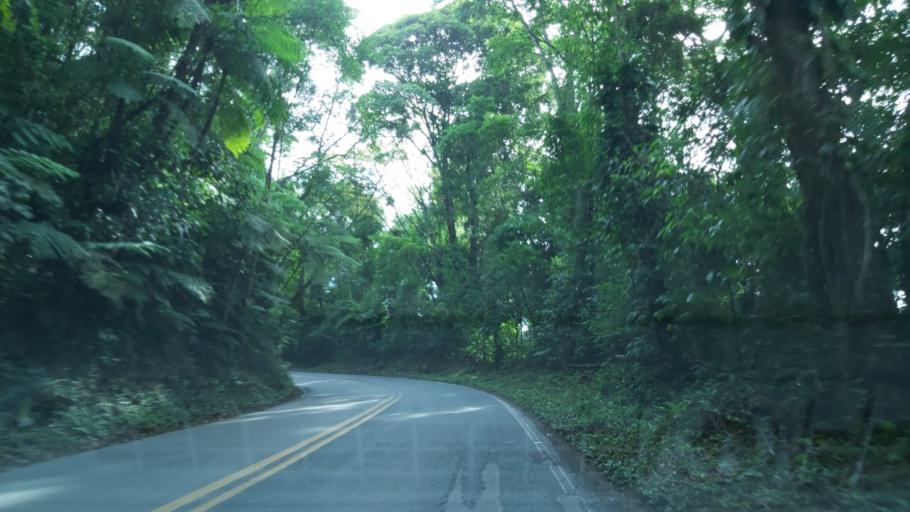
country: BR
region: Sao Paulo
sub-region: Juquia
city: Juquia
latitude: -24.0986
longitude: -47.6186
